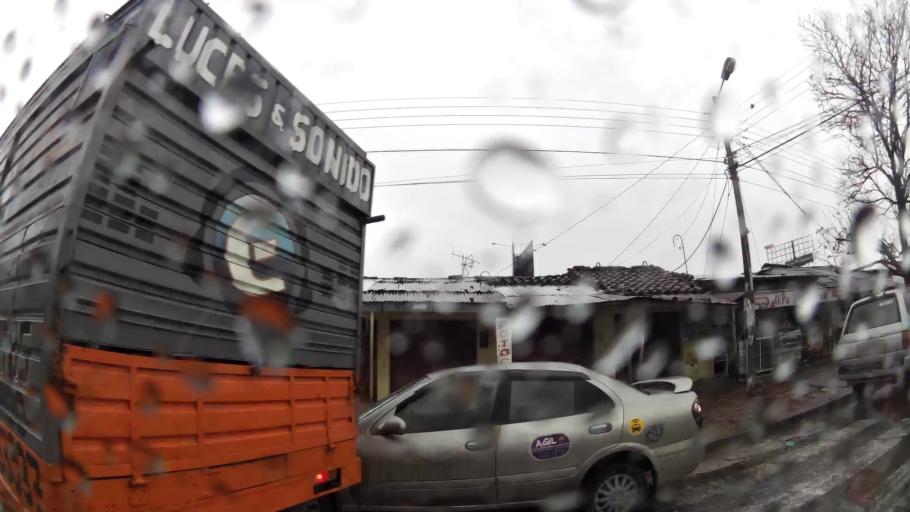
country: BO
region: Santa Cruz
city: Santa Cruz de la Sierra
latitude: -17.7839
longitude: -63.1957
